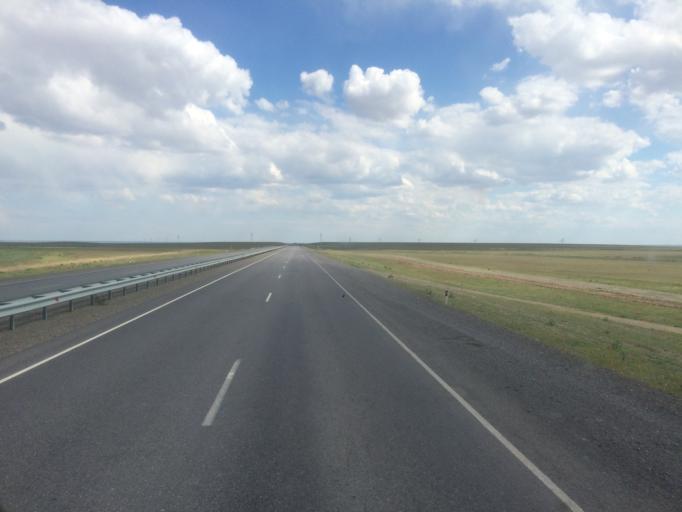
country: KZ
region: Qyzylorda
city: Shalqiya
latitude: 43.8635
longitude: 67.3959
